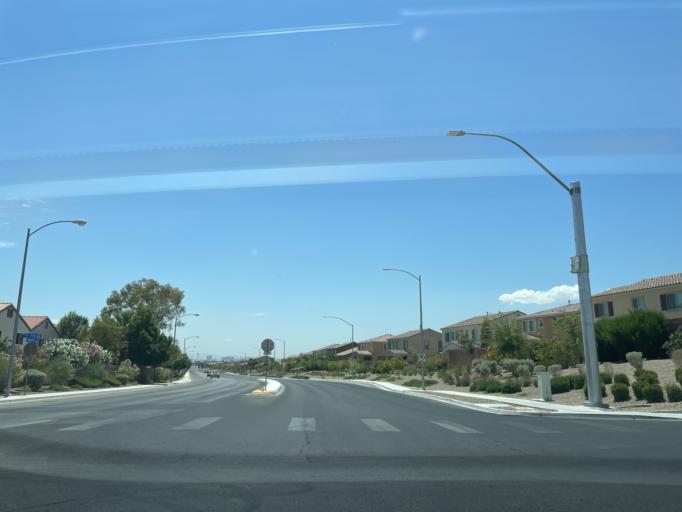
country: US
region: Nevada
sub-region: Clark County
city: North Las Vegas
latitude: 36.2839
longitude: -115.1530
